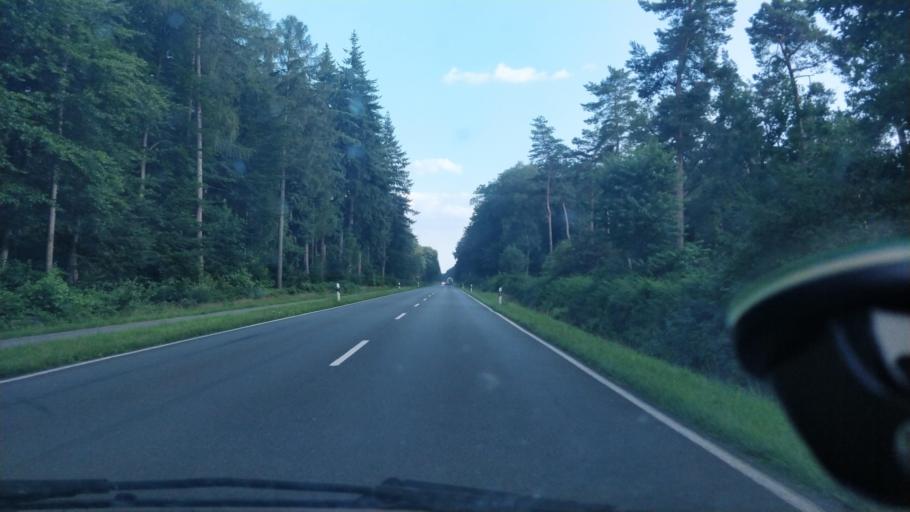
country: DE
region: North Rhine-Westphalia
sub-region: Regierungsbezirk Dusseldorf
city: Alpen
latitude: 51.5479
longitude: 6.5033
